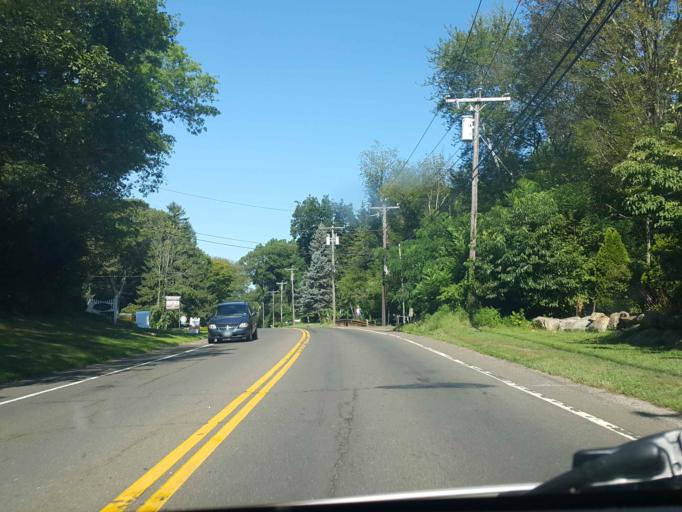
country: US
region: Connecticut
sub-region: New Haven County
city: North Branford
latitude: 41.3090
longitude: -72.7256
